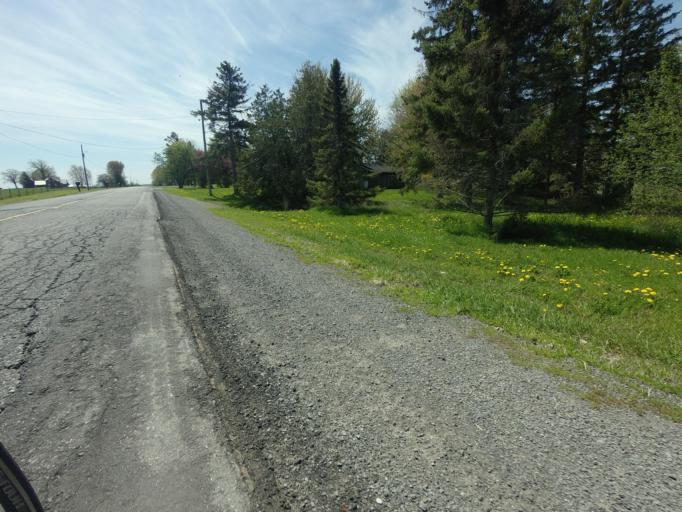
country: CA
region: Ontario
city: Arnprior
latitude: 45.3819
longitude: -76.1291
